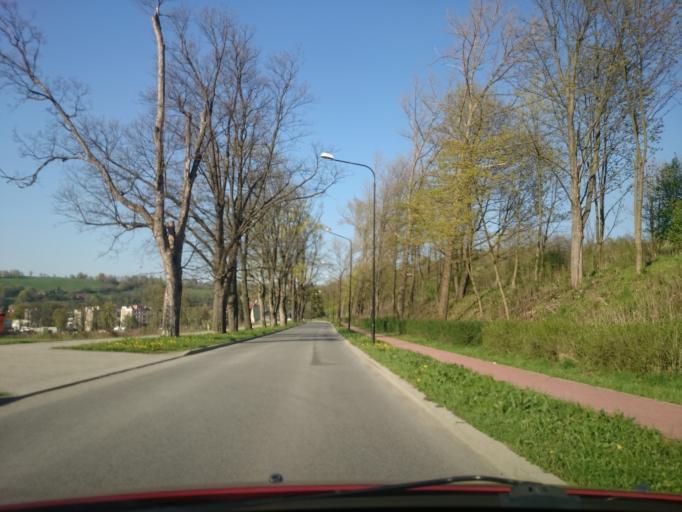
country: PL
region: Lower Silesian Voivodeship
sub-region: Powiat klodzki
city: Duszniki-Zdroj
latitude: 50.3972
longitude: 16.3897
